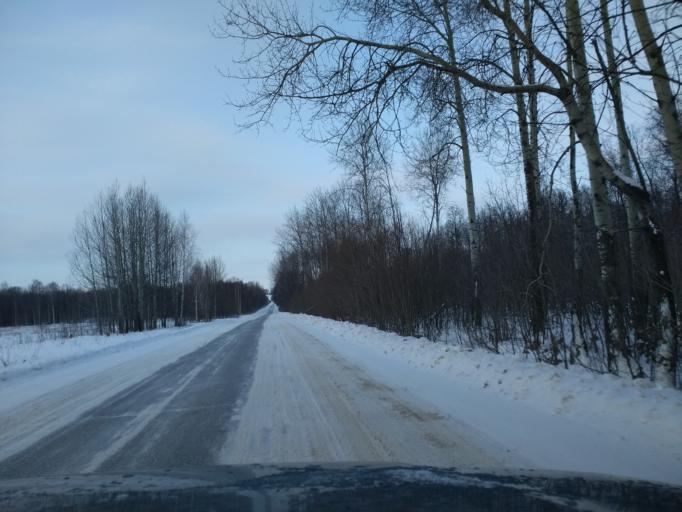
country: RU
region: Bashkortostan
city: Iglino
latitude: 54.7484
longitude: 56.5913
